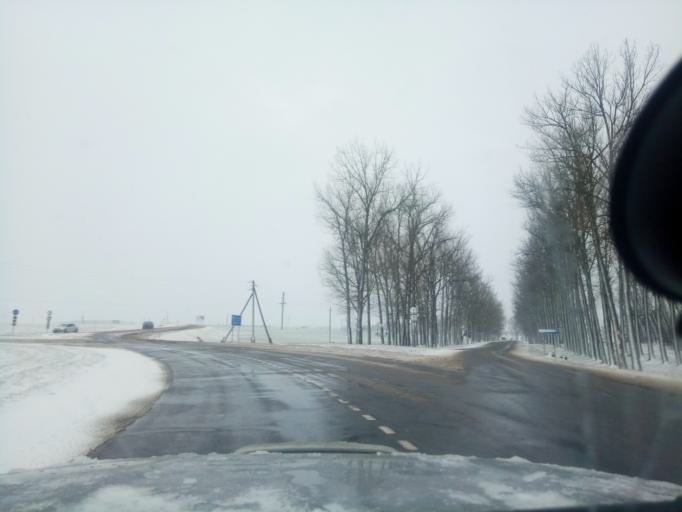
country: BY
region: Minsk
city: Haradzyeya
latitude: 53.3355
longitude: 26.5220
